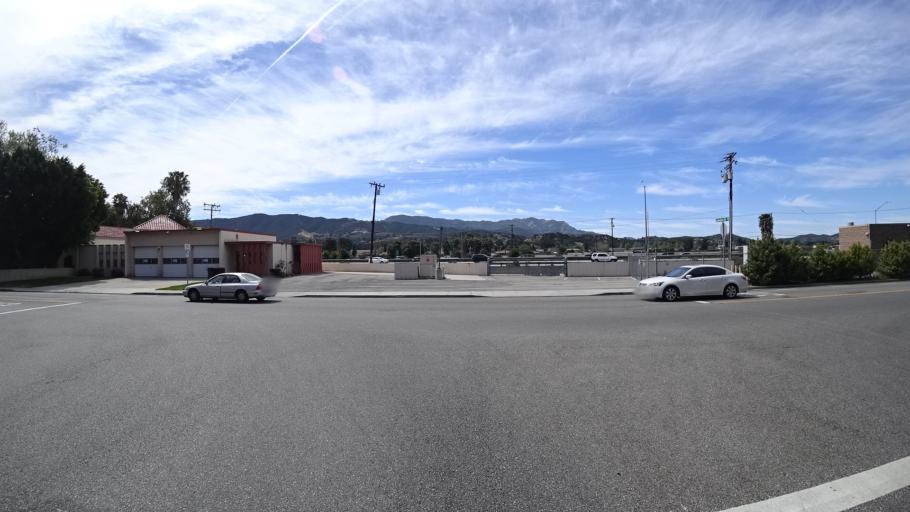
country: US
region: California
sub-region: Ventura County
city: Casa Conejo
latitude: 34.1866
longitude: -118.9300
